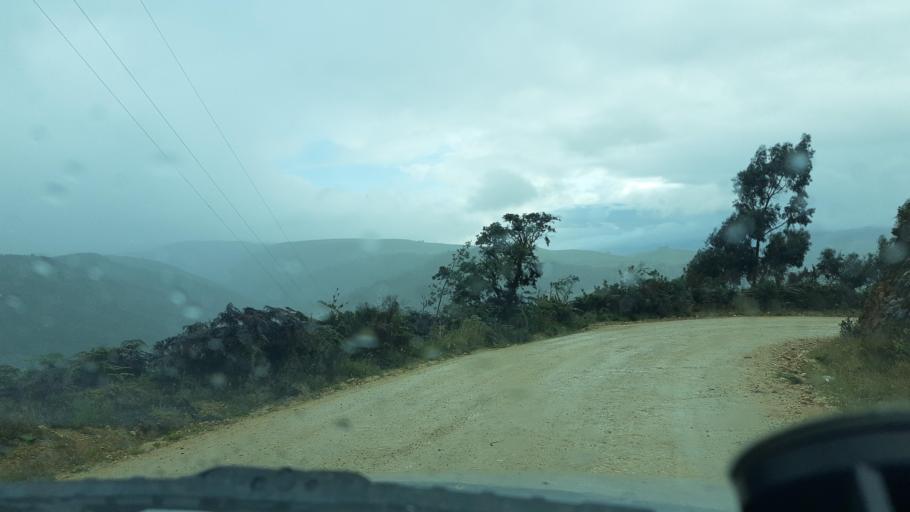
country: CO
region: Cundinamarca
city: Villapinzon
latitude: 5.2081
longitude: -73.5724
